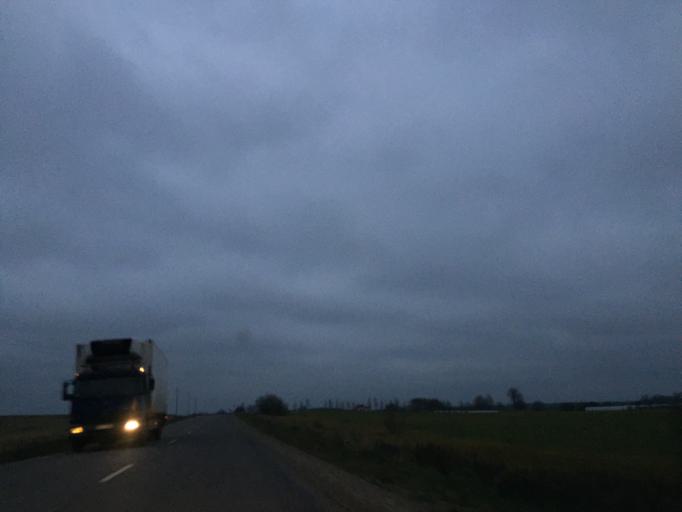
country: LV
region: Koceni
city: Koceni
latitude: 57.5497
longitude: 25.3126
